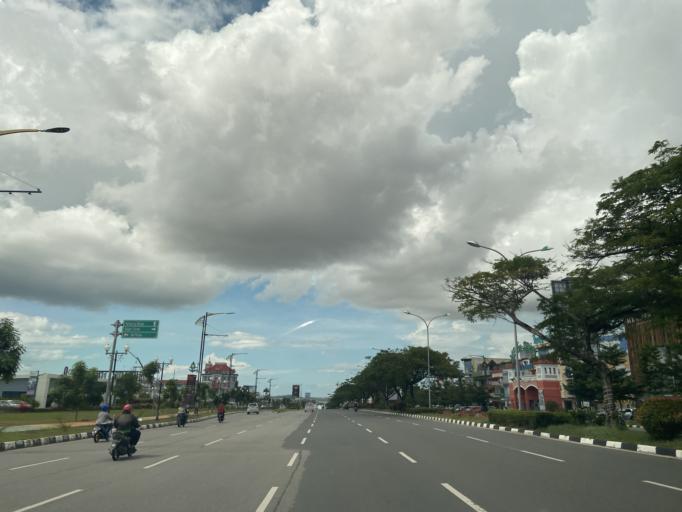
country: SG
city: Singapore
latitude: 1.1254
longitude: 104.0293
